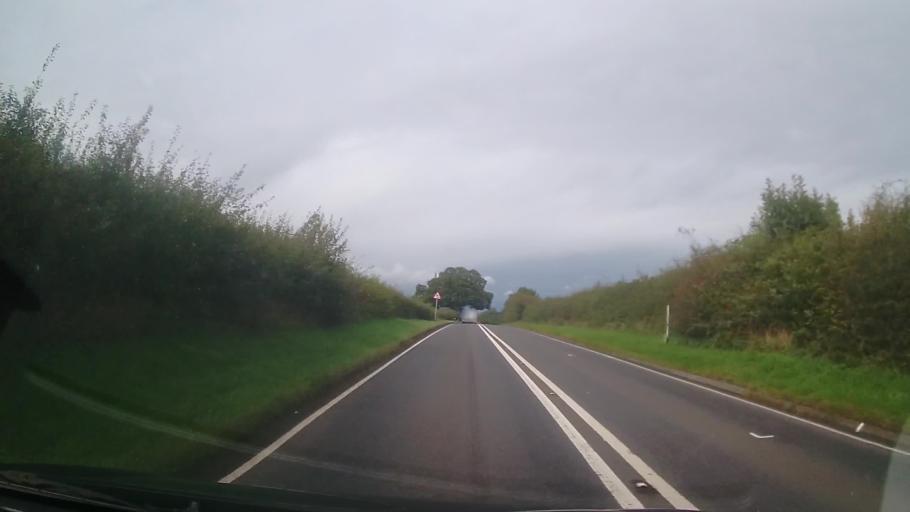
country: GB
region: England
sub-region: Shropshire
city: Romsley
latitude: 52.4305
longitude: -2.3119
